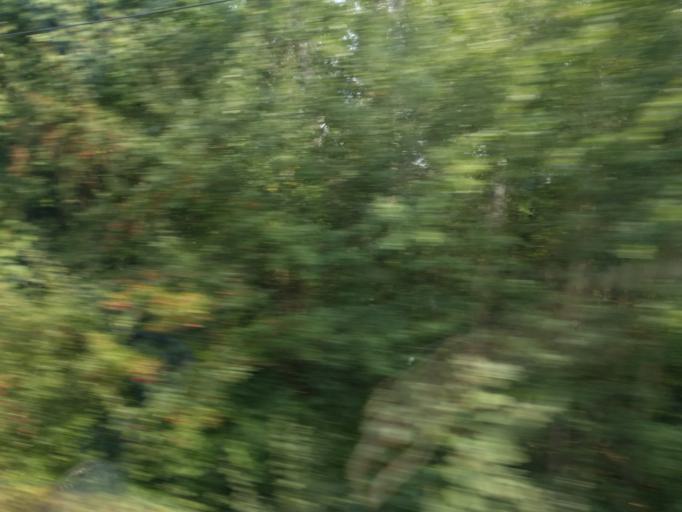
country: DE
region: Hamburg
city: Farmsen-Berne
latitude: 53.6118
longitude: 10.1615
